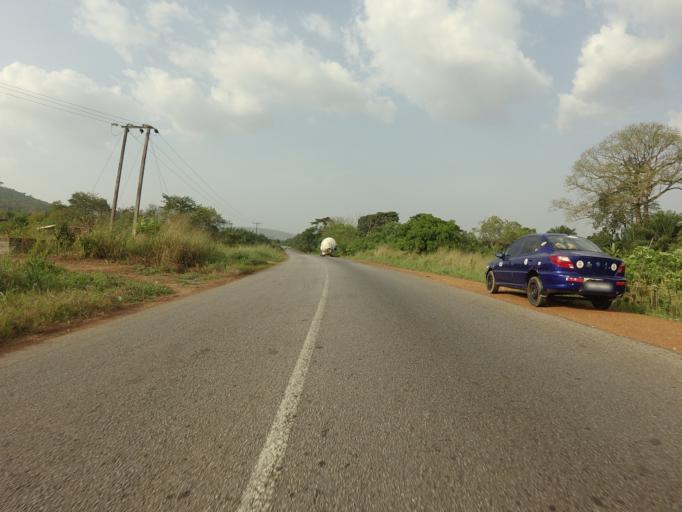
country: GH
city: Akropong
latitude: 6.2662
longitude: 0.1365
